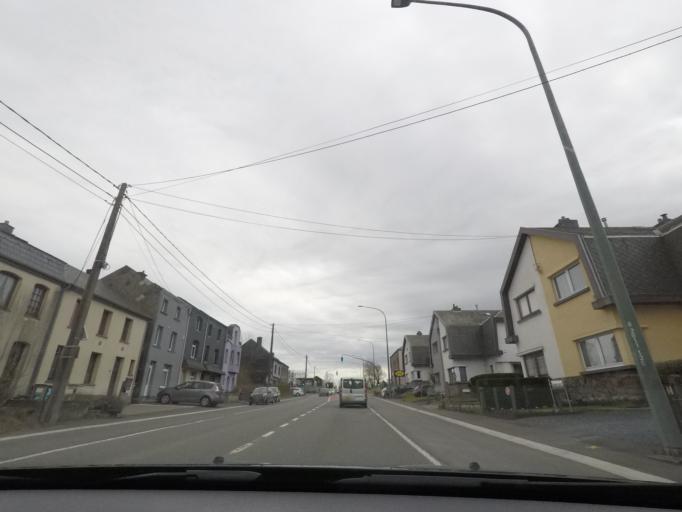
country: BE
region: Wallonia
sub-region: Province du Luxembourg
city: Bastogne
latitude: 49.9959
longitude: 5.7229
